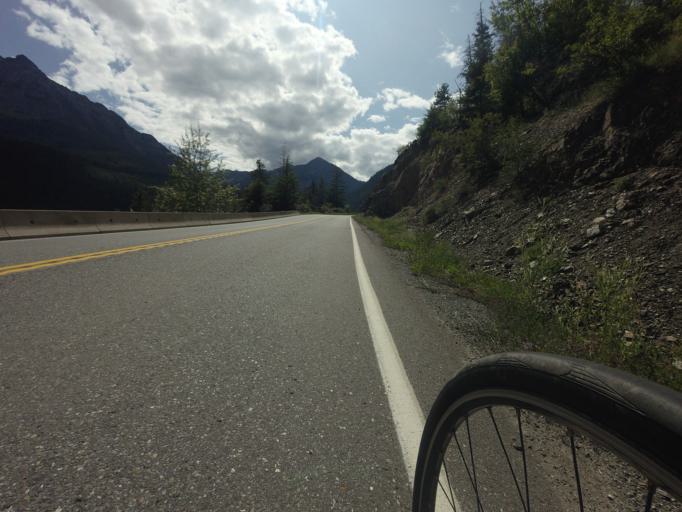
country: CA
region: British Columbia
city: Lillooet
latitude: 50.6533
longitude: -122.0024
